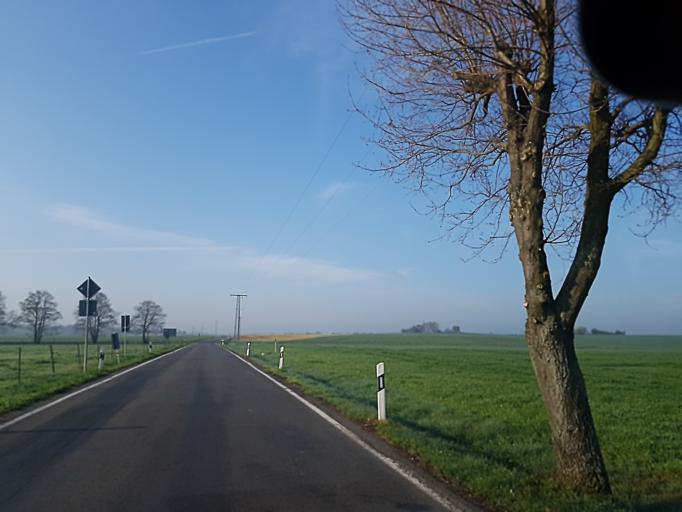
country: DE
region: Saxony
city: Cavertitz
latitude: 51.3880
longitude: 13.0971
